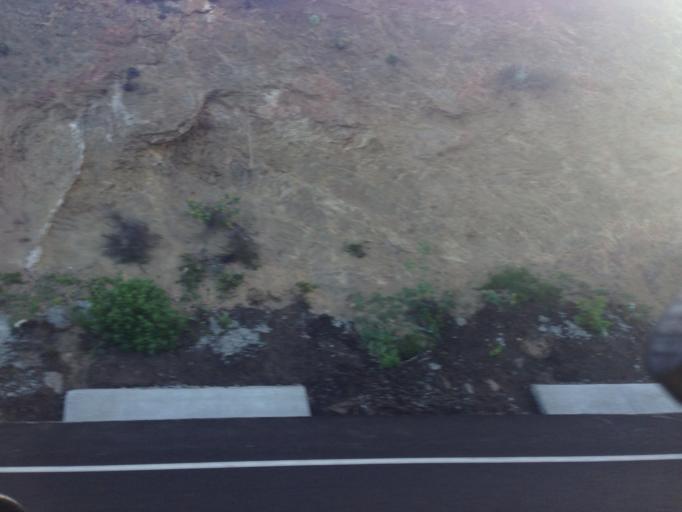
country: MX
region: Baja California
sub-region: Playas de Rosarito
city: Santa Anita
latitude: 32.1435
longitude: -116.8910
